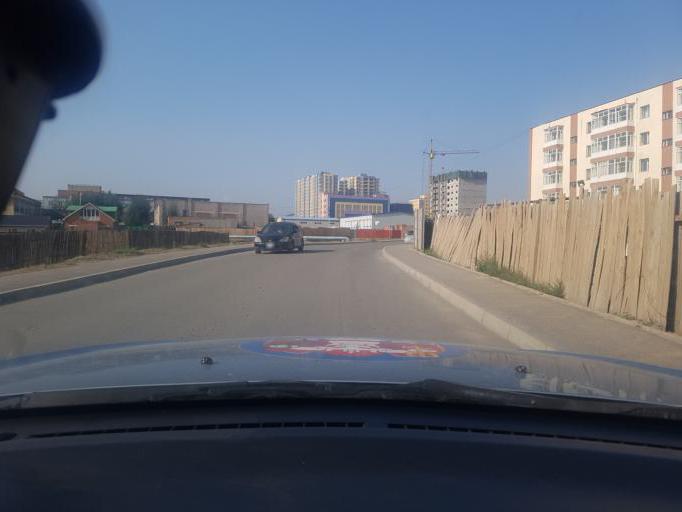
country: MN
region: Ulaanbaatar
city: Ulaanbaatar
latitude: 47.9206
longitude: 106.9651
